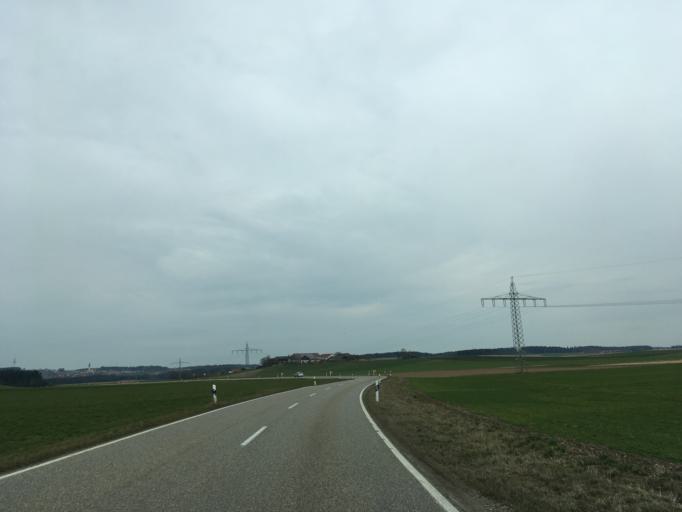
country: DE
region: Bavaria
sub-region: Upper Bavaria
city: Schnaitsee
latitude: 48.0352
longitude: 12.3716
